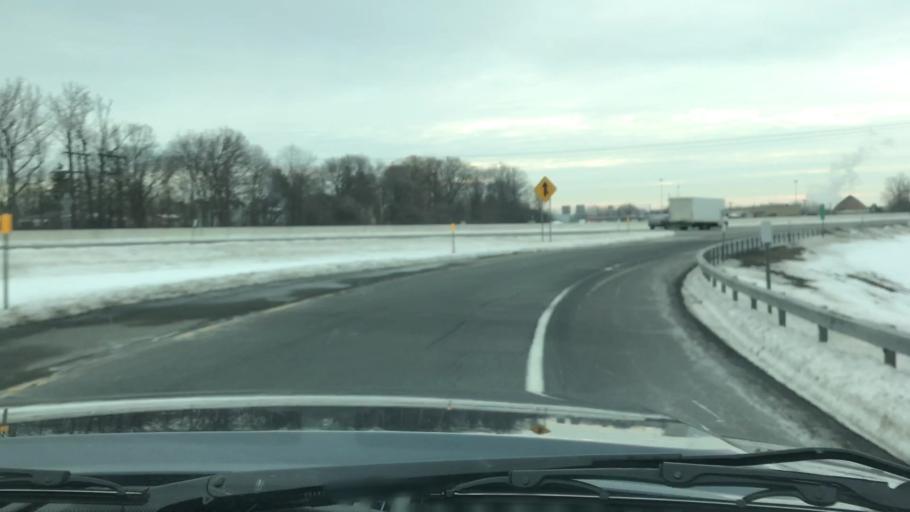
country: US
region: New York
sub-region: Albany County
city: Albany
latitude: 42.6338
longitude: -73.7837
